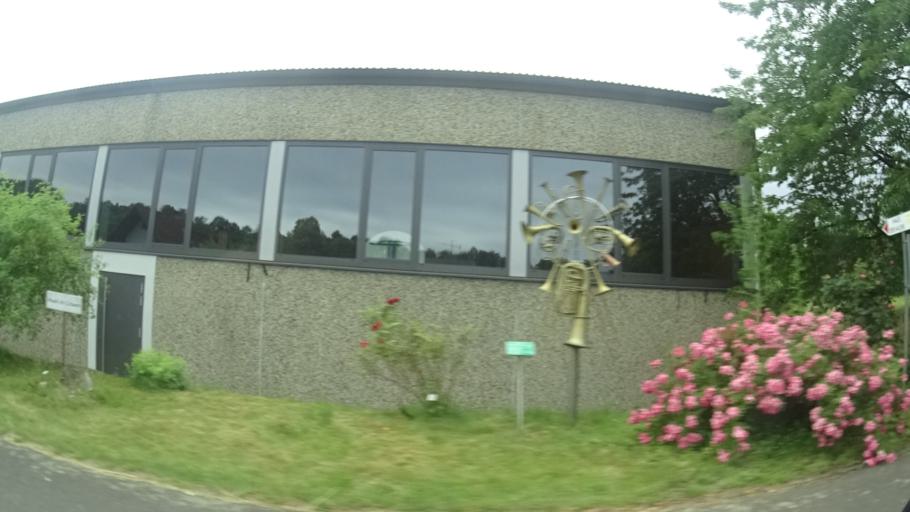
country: DE
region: Bavaria
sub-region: Regierungsbezirk Unterfranken
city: Johannesberg
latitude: 50.0568
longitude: 9.1324
